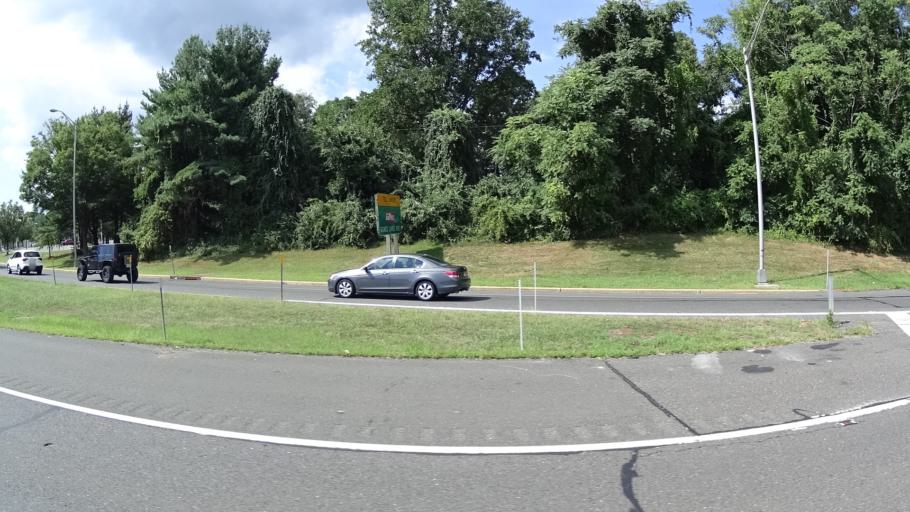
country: US
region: New Jersey
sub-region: Monmouth County
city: Lincroft
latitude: 40.3400
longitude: -74.1028
